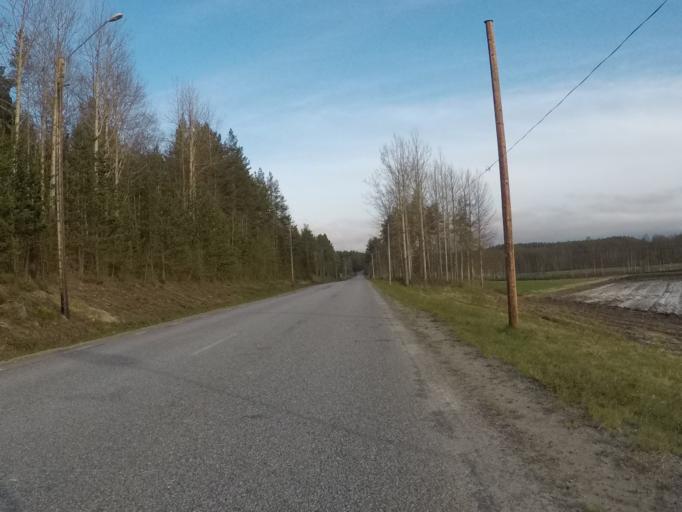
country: SE
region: Vaesterbotten
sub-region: Robertsfors Kommun
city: Robertsfors
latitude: 63.9966
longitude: 20.8067
